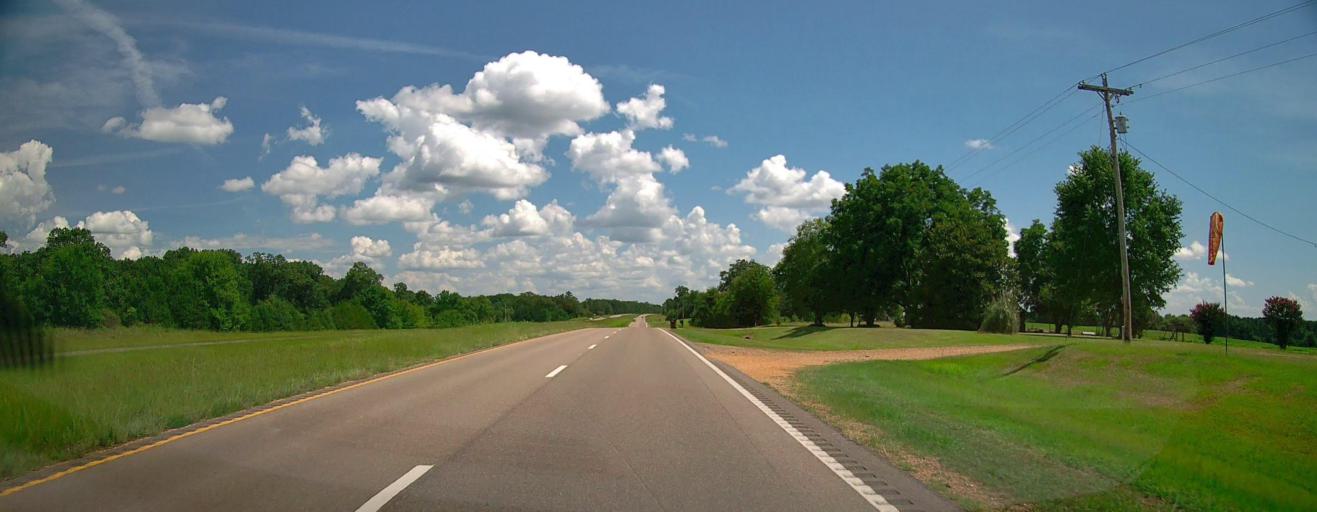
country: US
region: Mississippi
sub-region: Monroe County
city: Amory
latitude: 33.9495
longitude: -88.6028
